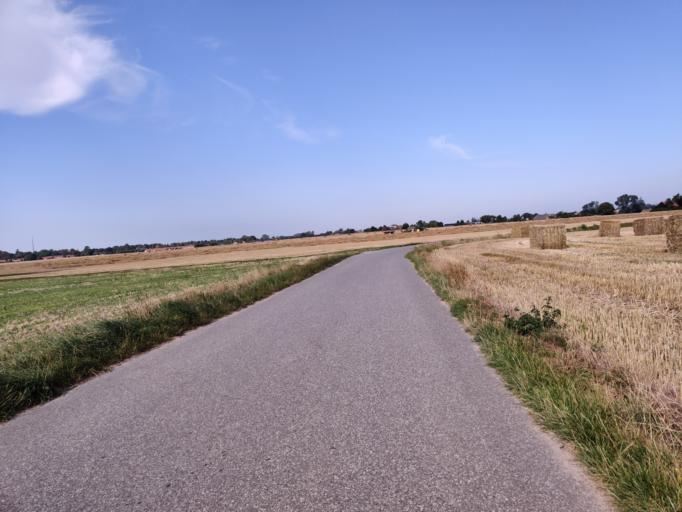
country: DK
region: Zealand
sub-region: Guldborgsund Kommune
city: Nykobing Falster
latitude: 54.6961
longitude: 11.9257
